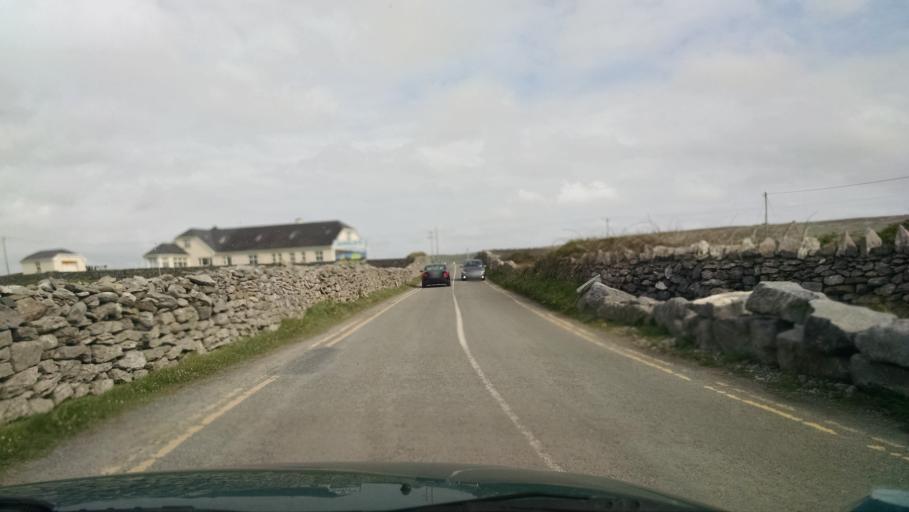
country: IE
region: Connaught
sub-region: County Galway
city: Bearna
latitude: 53.0162
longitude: -9.4019
